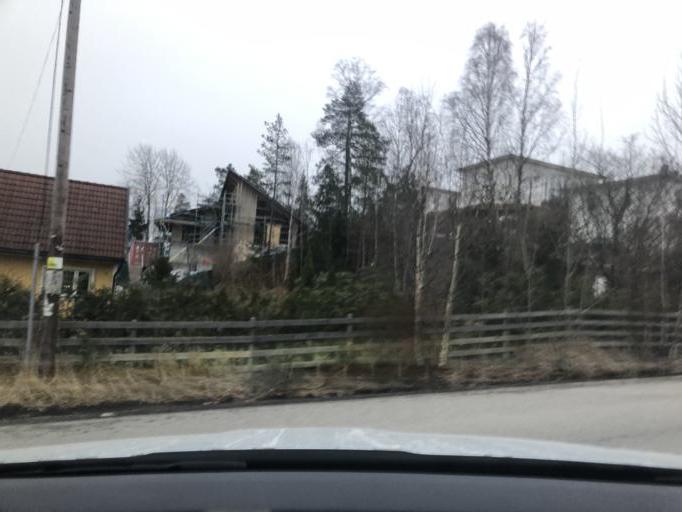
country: SE
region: Stockholm
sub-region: Botkyrka Kommun
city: Tullinge
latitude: 59.1953
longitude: 17.9004
